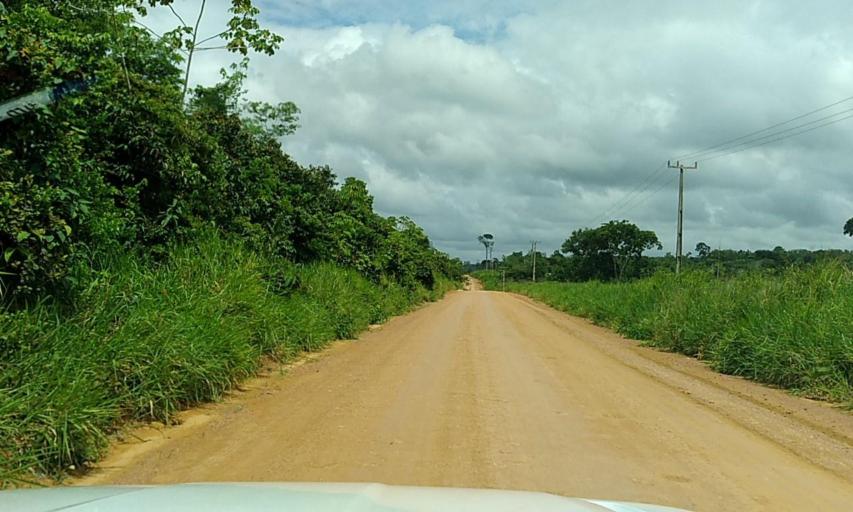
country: BR
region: Para
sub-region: Senador Jose Porfirio
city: Senador Jose Porfirio
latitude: -2.7765
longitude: -51.7770
